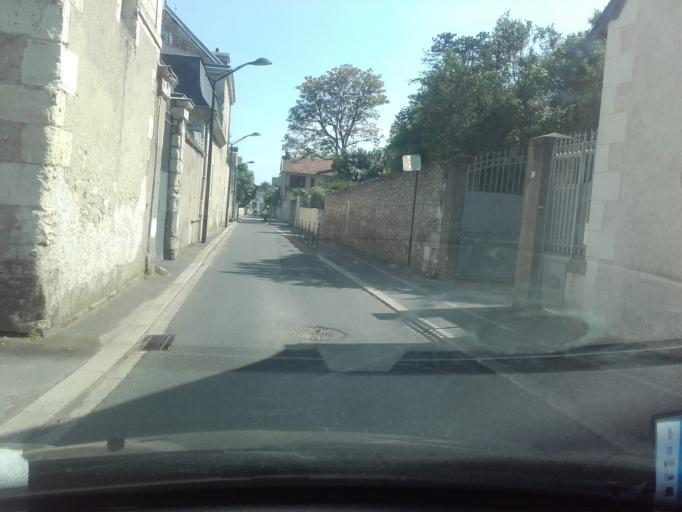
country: FR
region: Centre
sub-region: Departement d'Indre-et-Loire
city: Saint-Cyr-sur-Loire
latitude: 47.4143
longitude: 0.6758
